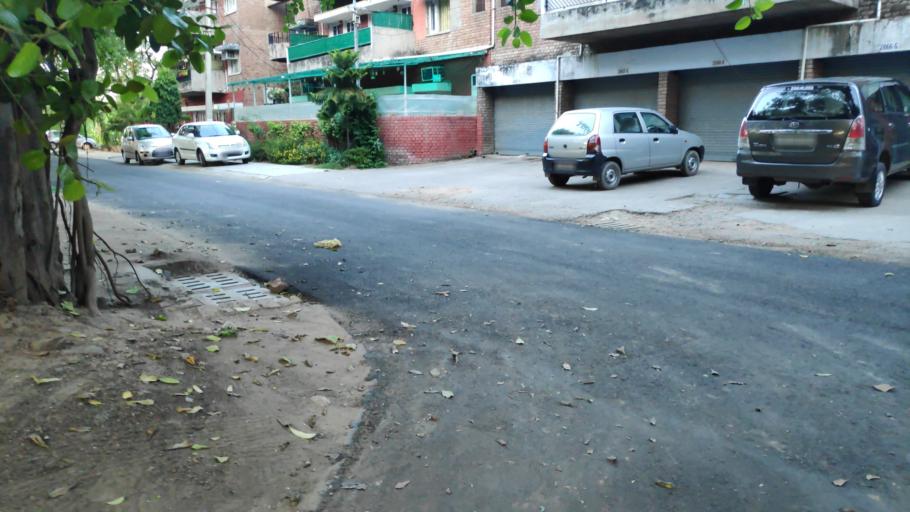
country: IN
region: Punjab
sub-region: Ajitgarh
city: Mohali
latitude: 30.7205
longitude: 76.7419
